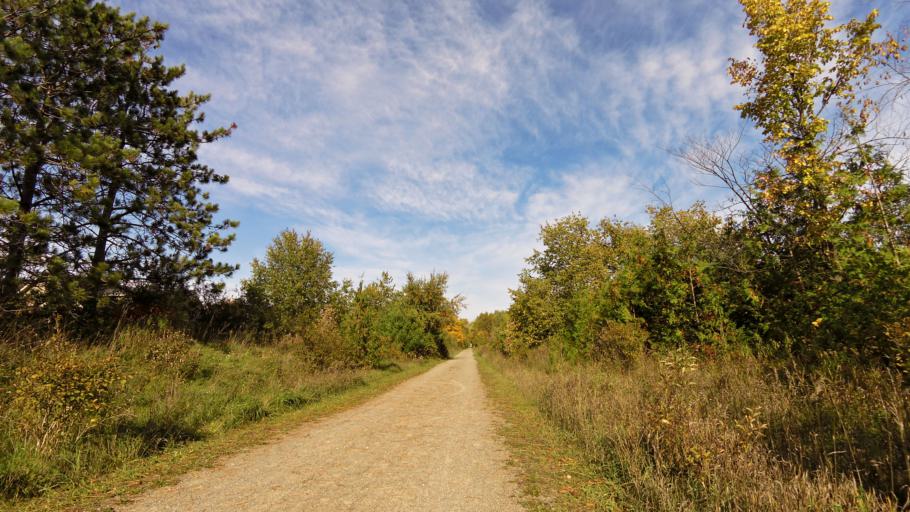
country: CA
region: Ontario
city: Orangeville
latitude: 43.7866
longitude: -80.0555
